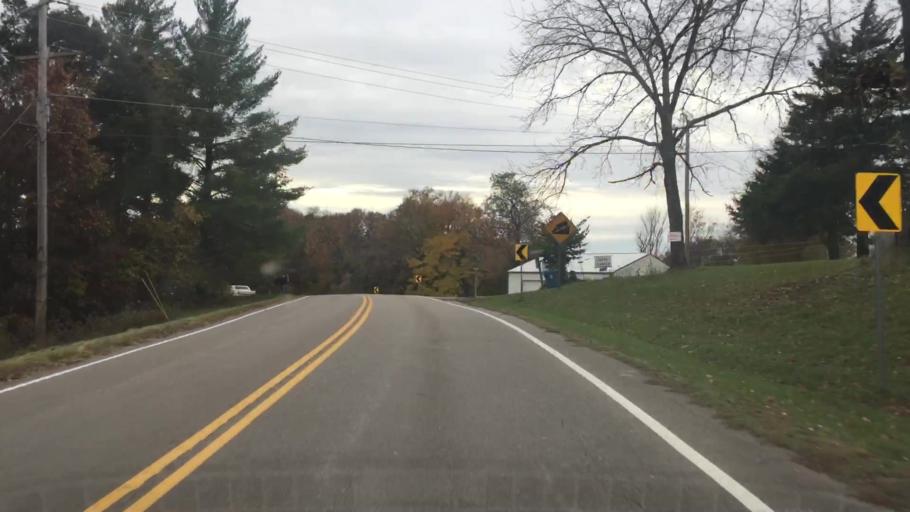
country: US
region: Missouri
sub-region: Osage County
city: Linn
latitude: 38.7144
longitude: -91.7133
